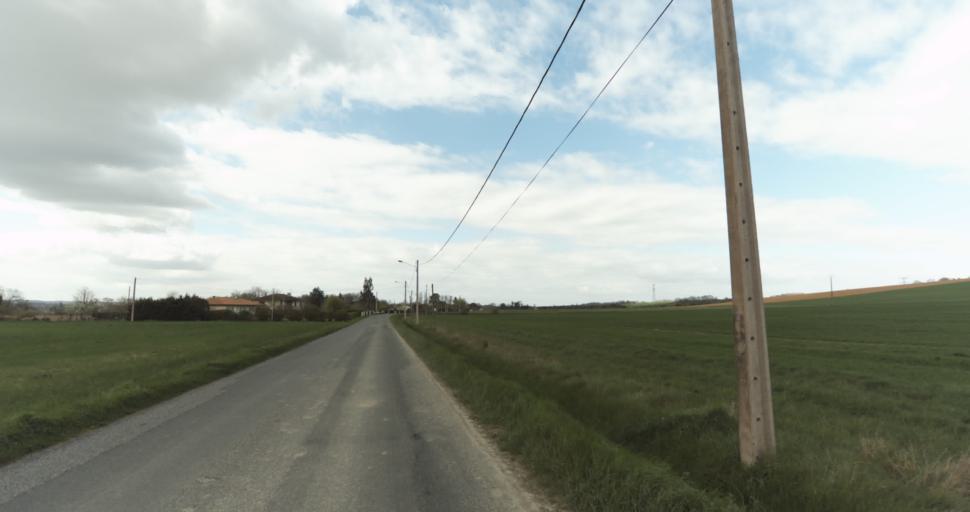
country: FR
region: Midi-Pyrenees
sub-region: Departement de la Haute-Garonne
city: Auterive
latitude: 43.3751
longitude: 1.4650
